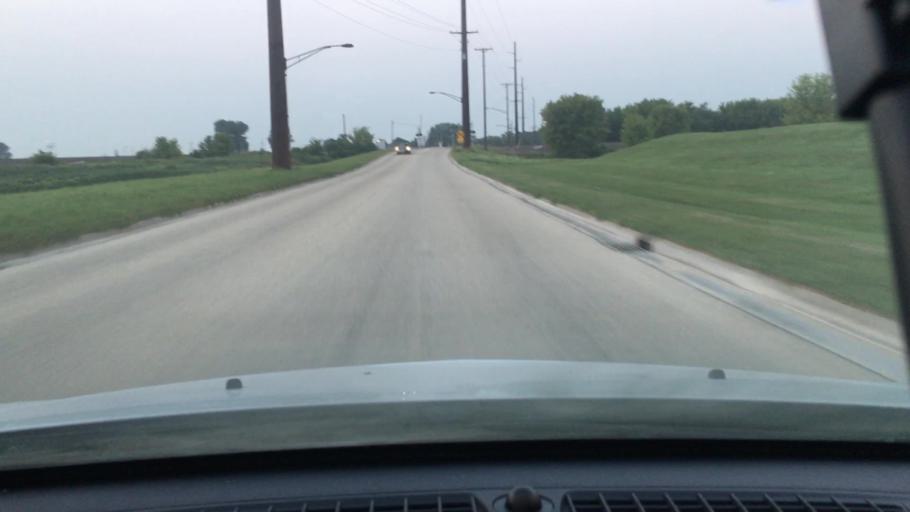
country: US
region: Illinois
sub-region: Ogle County
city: Rochelle
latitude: 41.9239
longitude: -89.0544
